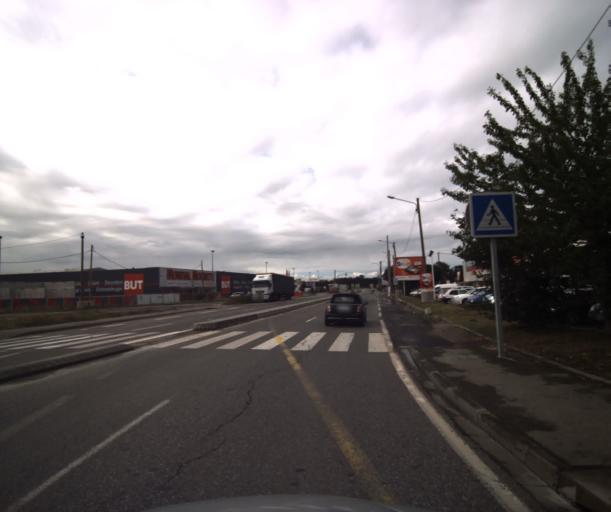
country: FR
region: Midi-Pyrenees
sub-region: Departement de la Haute-Garonne
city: Portet-sur-Garonne
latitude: 43.5484
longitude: 1.4198
